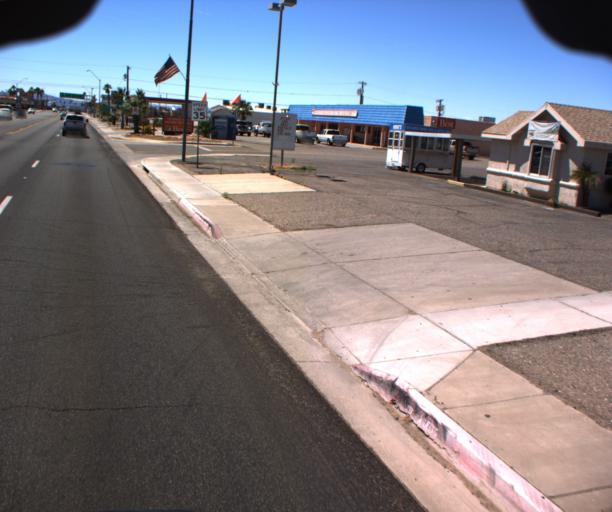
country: US
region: Arizona
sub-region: La Paz County
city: Parker
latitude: 34.1523
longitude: -114.2848
